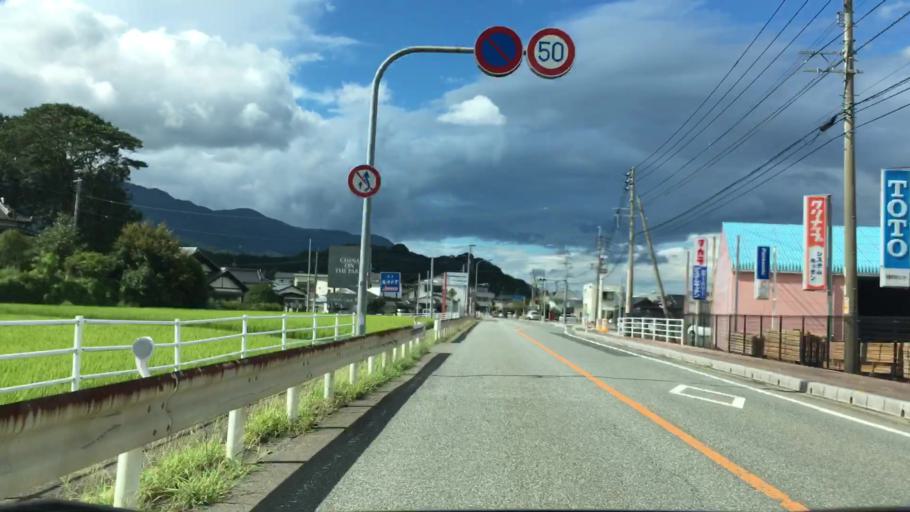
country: JP
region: Saga Prefecture
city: Imaricho-ko
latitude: 33.1919
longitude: 129.8513
